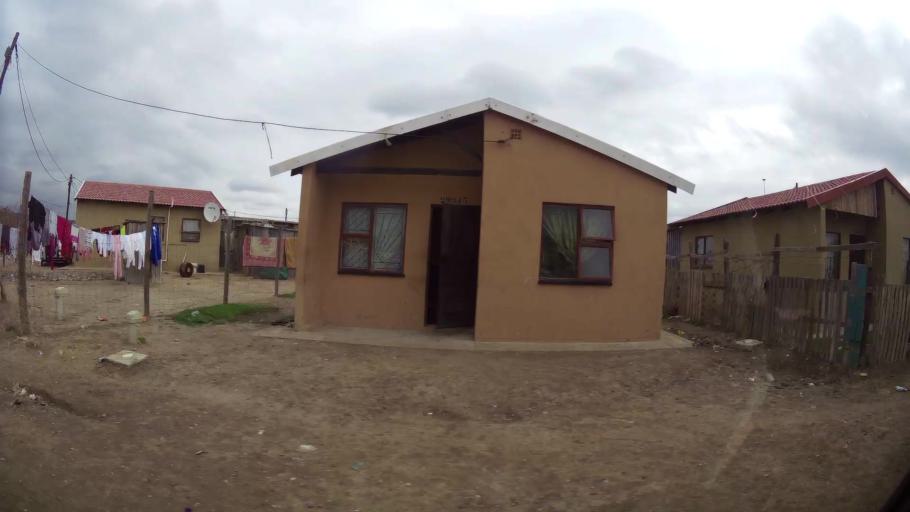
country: ZA
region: Eastern Cape
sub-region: Nelson Mandela Bay Metropolitan Municipality
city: Port Elizabeth
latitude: -33.8850
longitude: 25.5546
